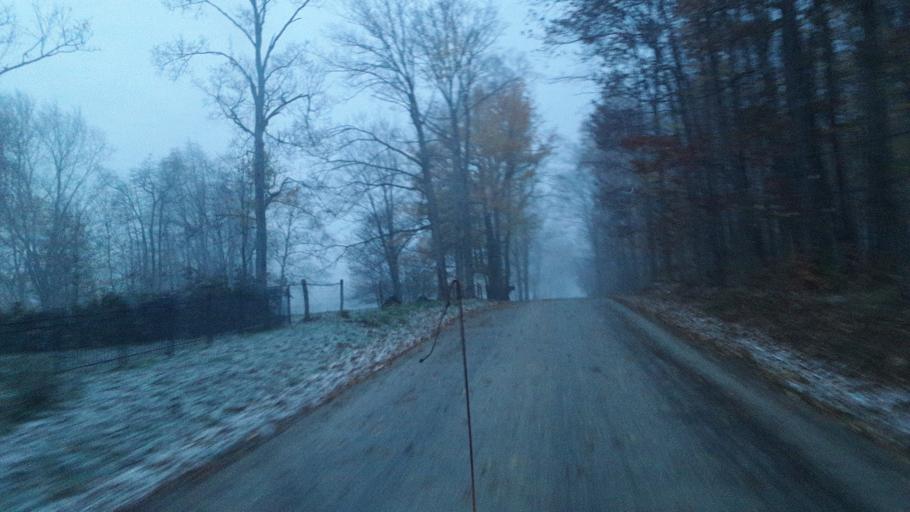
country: US
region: Ohio
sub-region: Geauga County
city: Middlefield
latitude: 41.4098
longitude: -81.1042
